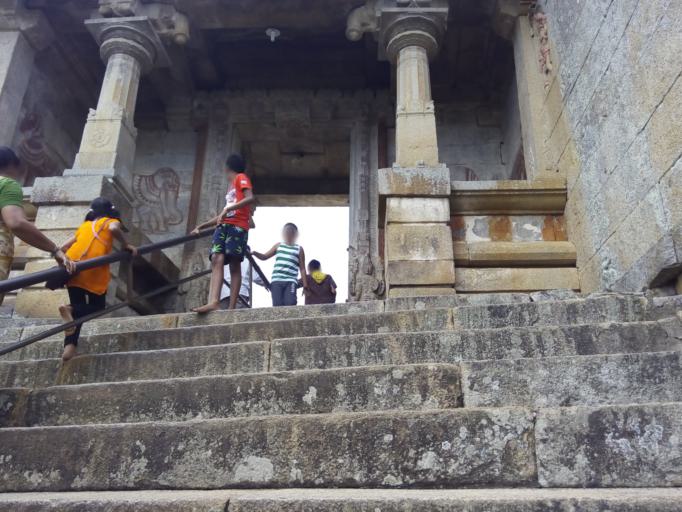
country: IN
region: Karnataka
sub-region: Hassan
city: Shravanabelagola
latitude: 12.8544
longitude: 76.4848
